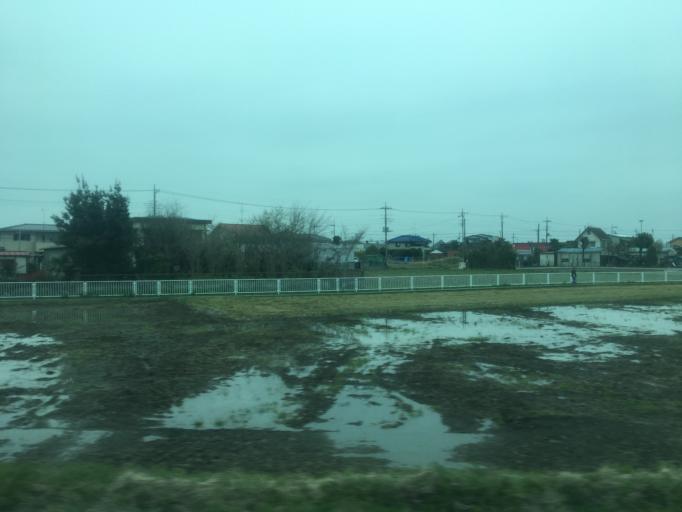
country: JP
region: Saitama
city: Fukiage-fujimi
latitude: 36.1213
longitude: 139.4226
